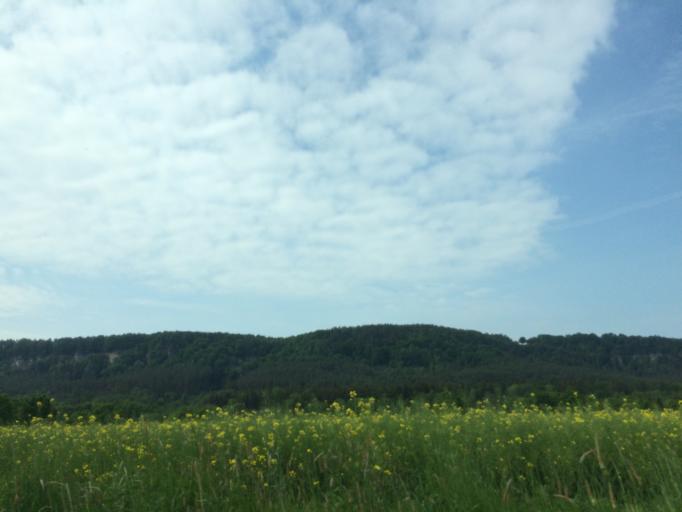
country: CZ
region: Central Bohemia
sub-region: Okres Mlada Boleslav
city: Zd'ar
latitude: 50.5417
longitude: 15.0610
